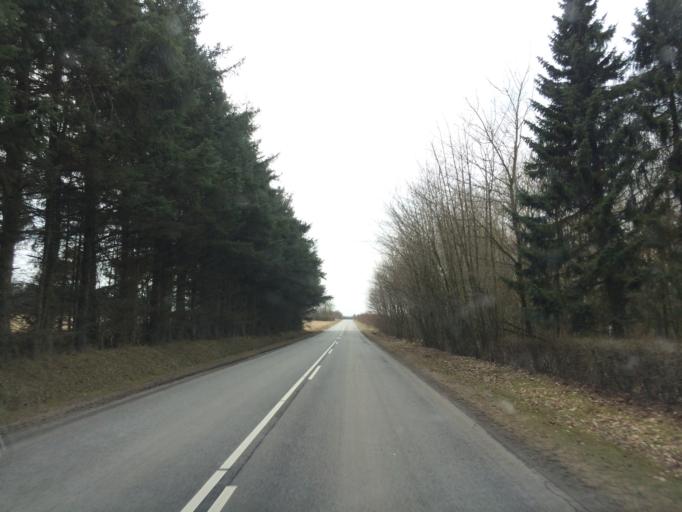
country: DK
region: Central Jutland
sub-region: Ringkobing-Skjern Kommune
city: Tarm
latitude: 55.8449
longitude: 8.4762
